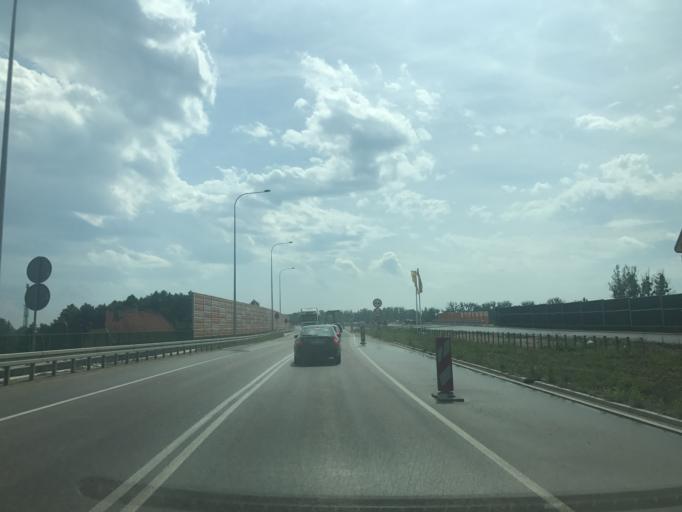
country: PL
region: Warmian-Masurian Voivodeship
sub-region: Powiat ostrodzki
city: Ostroda
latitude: 53.7058
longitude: 19.9781
